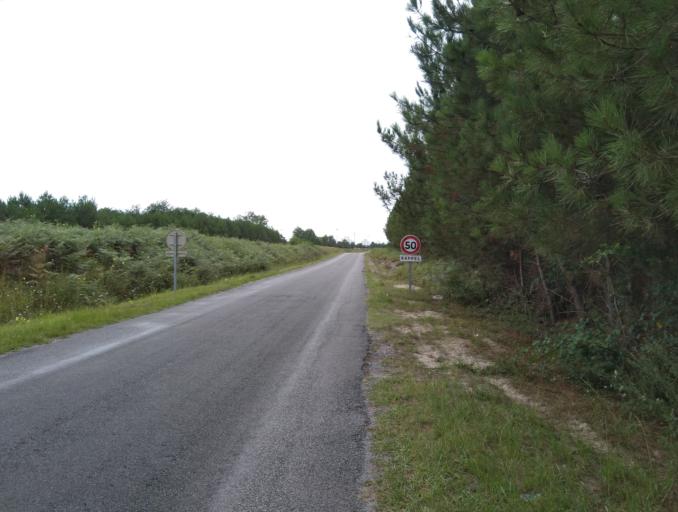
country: FR
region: Aquitaine
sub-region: Departement des Landes
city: Saint-Paul-les-Dax
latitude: 43.7399
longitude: -1.0820
